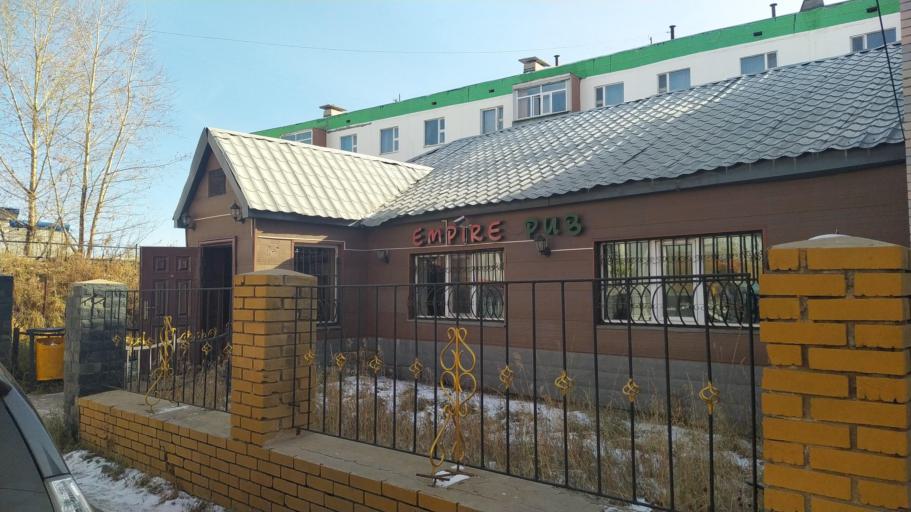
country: MN
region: Orhon
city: Erdenet
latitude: 49.0303
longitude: 104.0574
